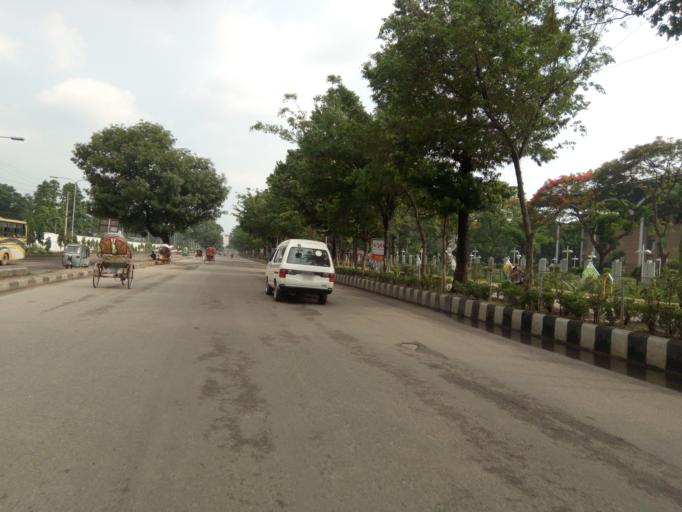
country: BD
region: Dhaka
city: Azimpur
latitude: 23.7701
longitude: 90.3826
